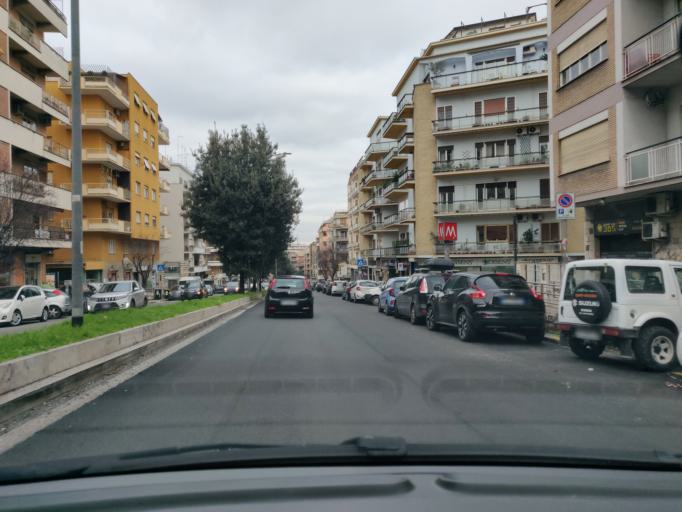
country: VA
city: Vatican City
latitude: 41.8986
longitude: 12.4321
